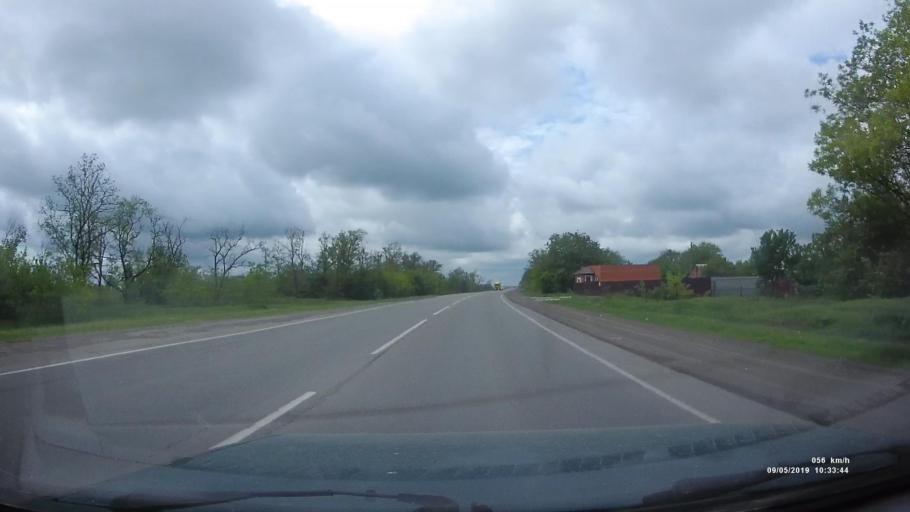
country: RU
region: Rostov
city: Azov
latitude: 47.0613
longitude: 39.4241
